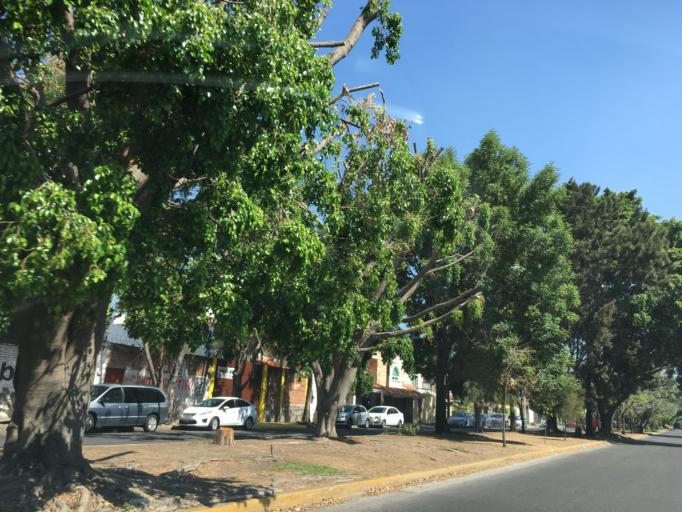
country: MX
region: Jalisco
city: Guadalajara
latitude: 20.6417
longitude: -103.3908
